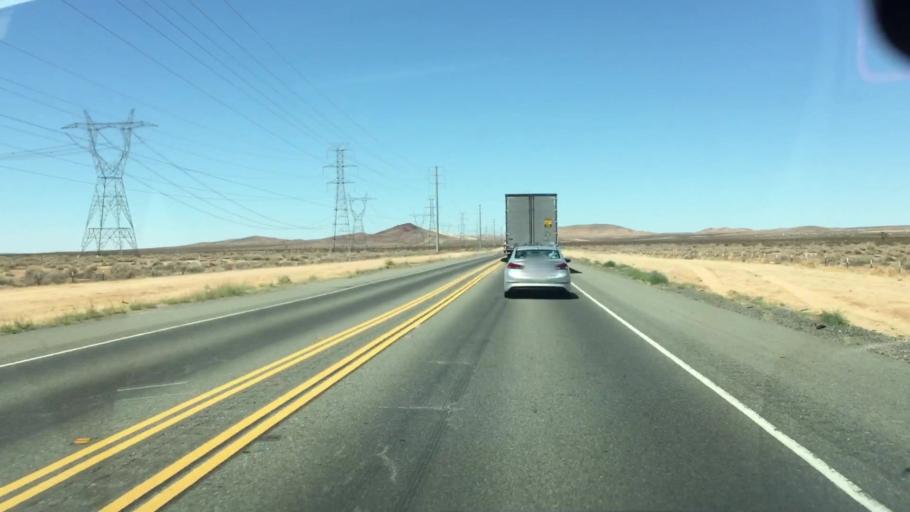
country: US
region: California
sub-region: Kern County
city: Boron
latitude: 34.8352
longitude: -117.4980
